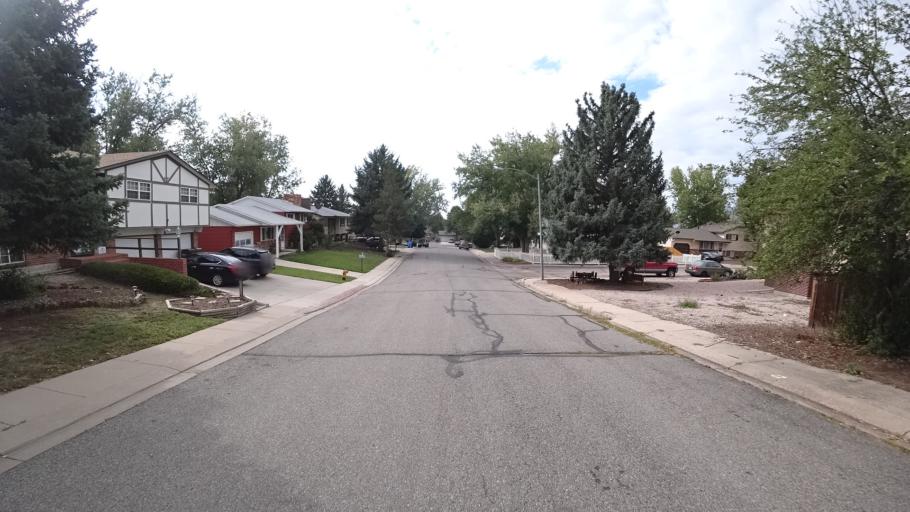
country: US
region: Colorado
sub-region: El Paso County
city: Cimarron Hills
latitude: 38.8554
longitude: -104.7431
